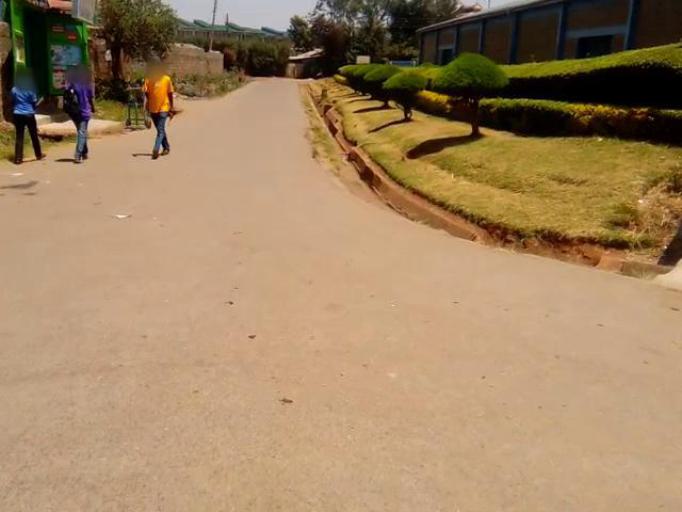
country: KE
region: Nairobi Area
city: Nairobi
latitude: -1.3122
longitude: 36.7760
